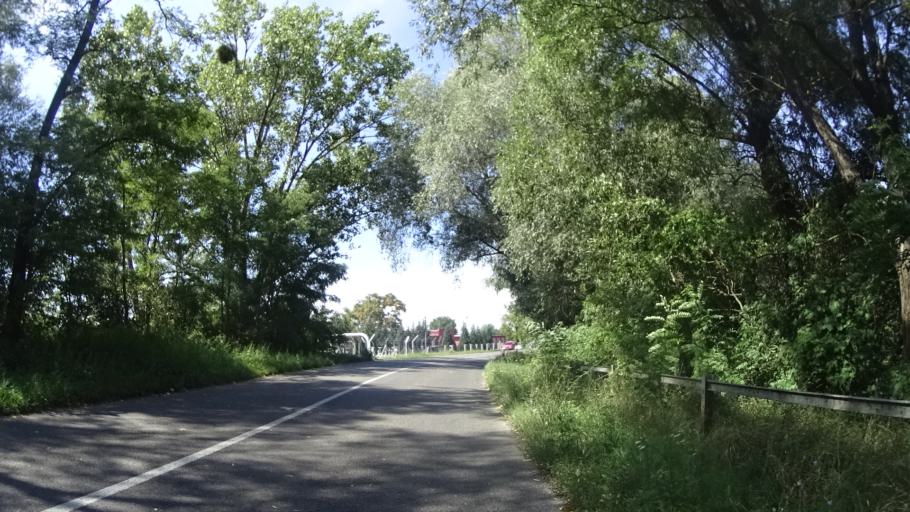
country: AT
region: Lower Austria
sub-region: Politischer Bezirk Ganserndorf
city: Marchegg
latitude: 48.3339
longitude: 16.9038
